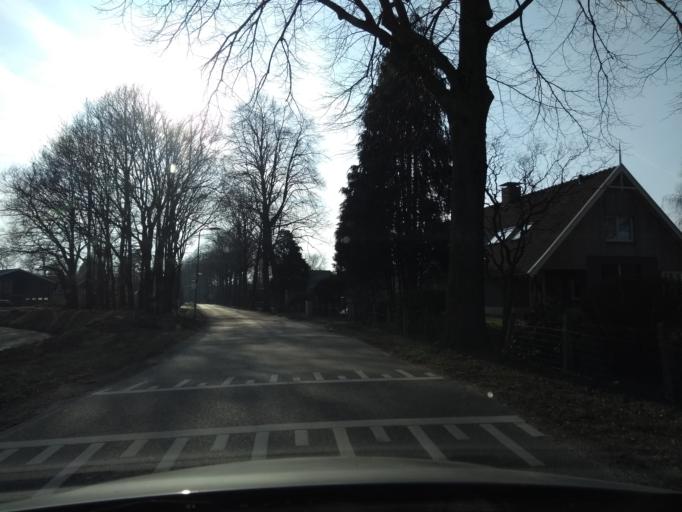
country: NL
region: Overijssel
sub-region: Gemeente Hengelo
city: Hengelo
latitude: 52.2693
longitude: 6.8340
